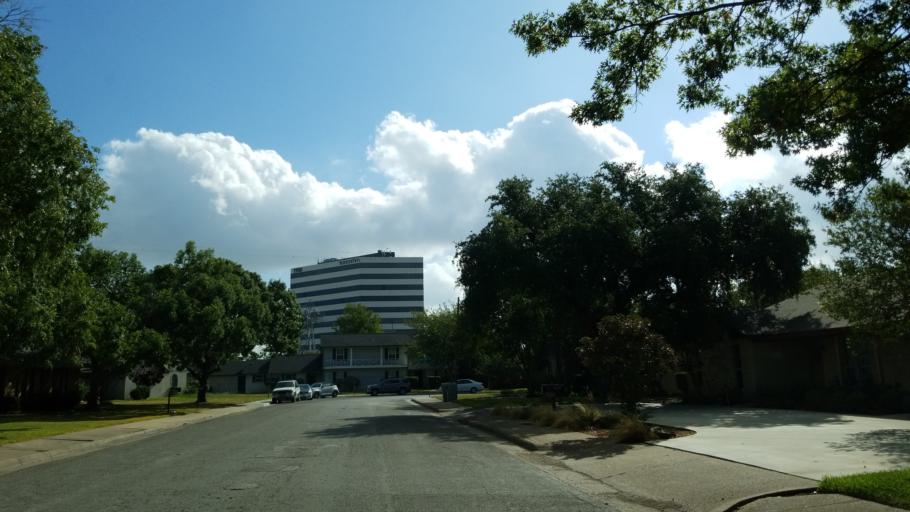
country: US
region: Texas
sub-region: Dallas County
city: Richardson
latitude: 32.9498
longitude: -96.7729
